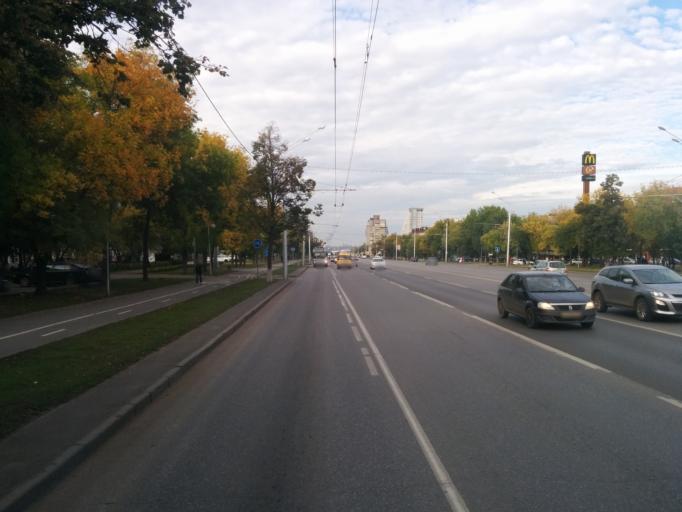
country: RU
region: Bashkortostan
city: Ufa
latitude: 54.7785
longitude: 56.0306
